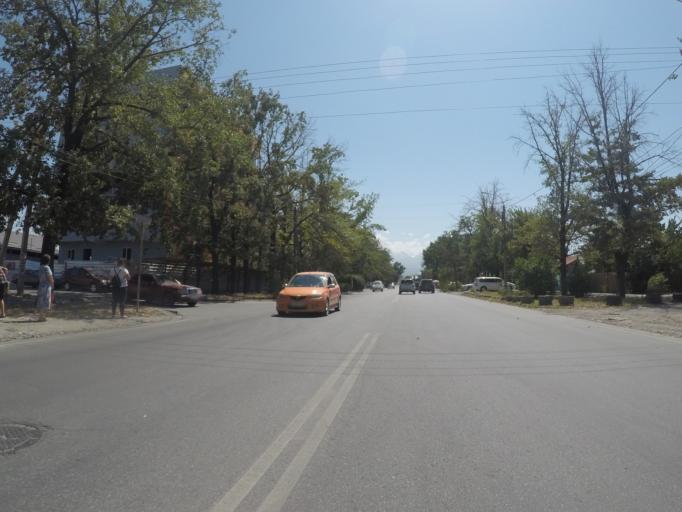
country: KG
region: Chuy
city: Bishkek
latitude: 42.8459
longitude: 74.5769
